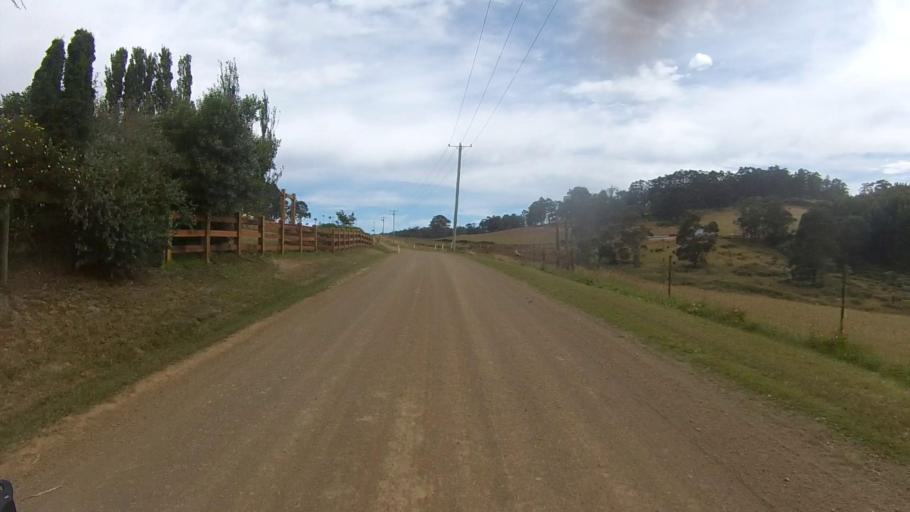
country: AU
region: Tasmania
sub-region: Sorell
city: Sorell
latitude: -42.7256
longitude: 147.7537
